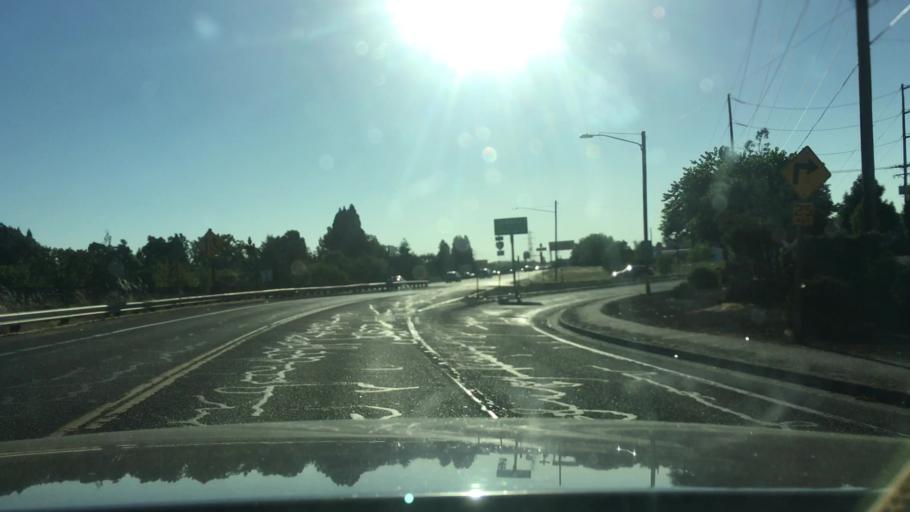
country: US
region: Oregon
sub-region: Lane County
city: Springfield
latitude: 44.0622
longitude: -123.0290
